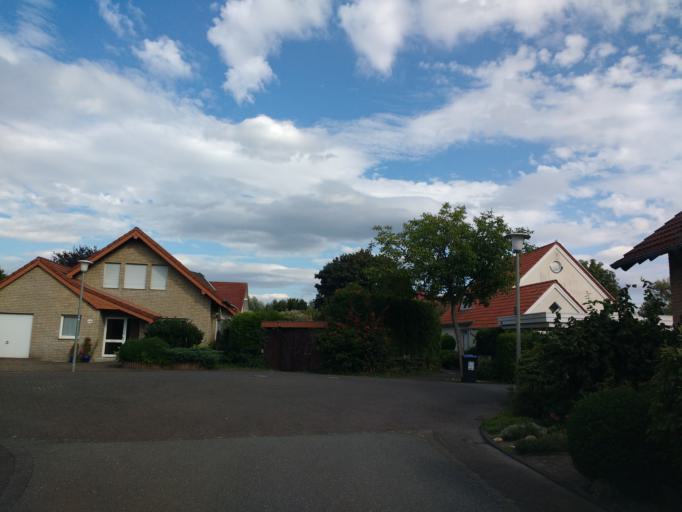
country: DE
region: North Rhine-Westphalia
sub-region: Regierungsbezirk Detmold
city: Schlangen
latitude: 51.7951
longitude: 8.8404
